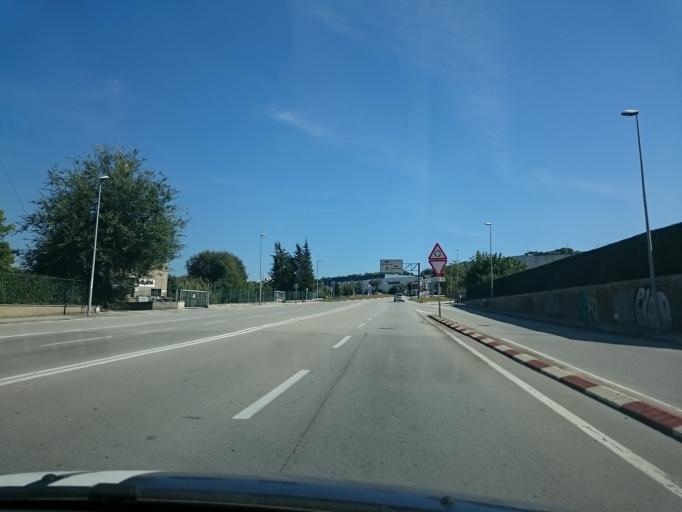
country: ES
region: Catalonia
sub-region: Provincia de Barcelona
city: Llica de Vall
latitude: 41.5879
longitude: 2.2549
